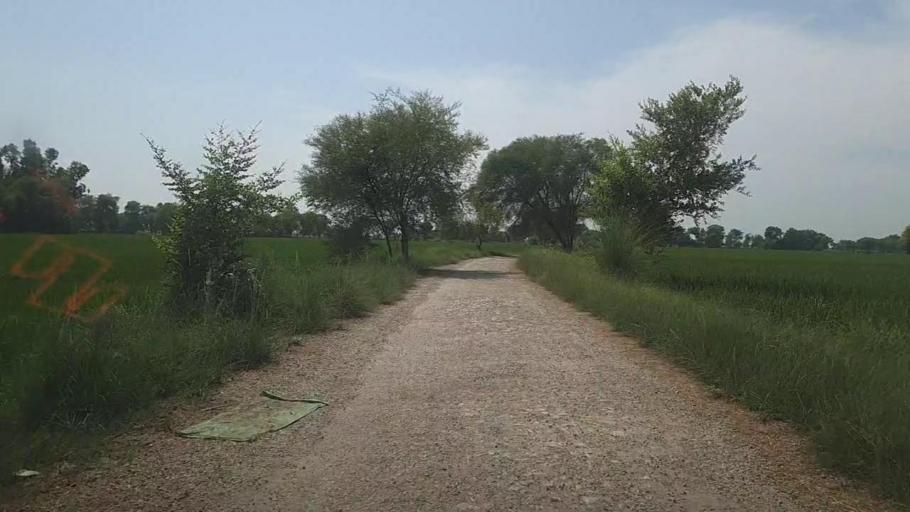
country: PK
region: Sindh
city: Kandhkot
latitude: 28.3109
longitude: 69.1985
